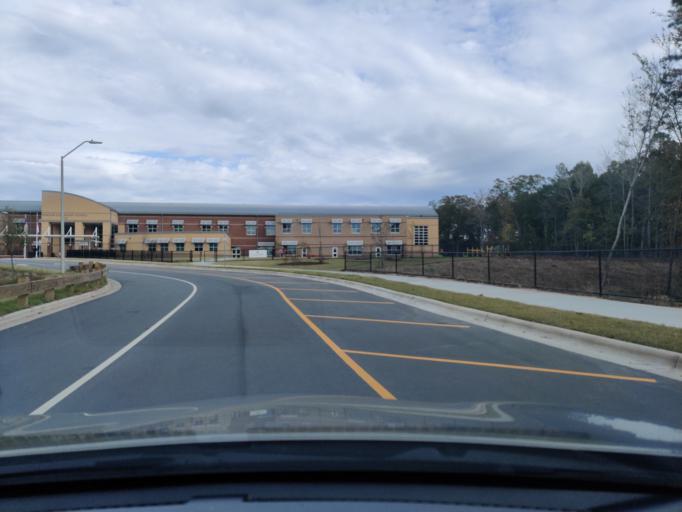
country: US
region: North Carolina
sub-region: Wake County
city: Morrisville
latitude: 35.8418
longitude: -78.8611
